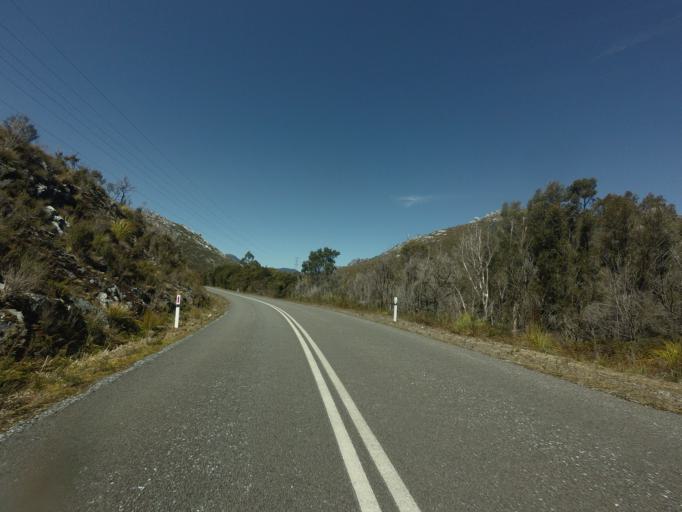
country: AU
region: Tasmania
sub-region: Huon Valley
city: Geeveston
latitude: -42.8500
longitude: 146.1758
